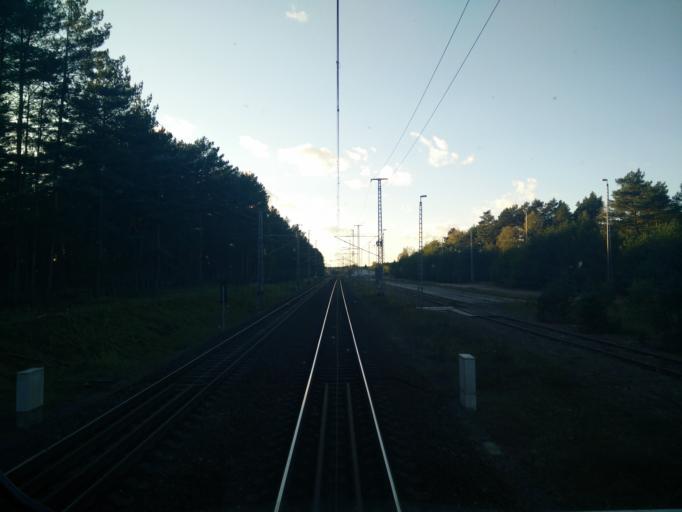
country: DE
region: Saxony-Anhalt
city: Havelberg
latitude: 52.9010
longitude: 12.0953
